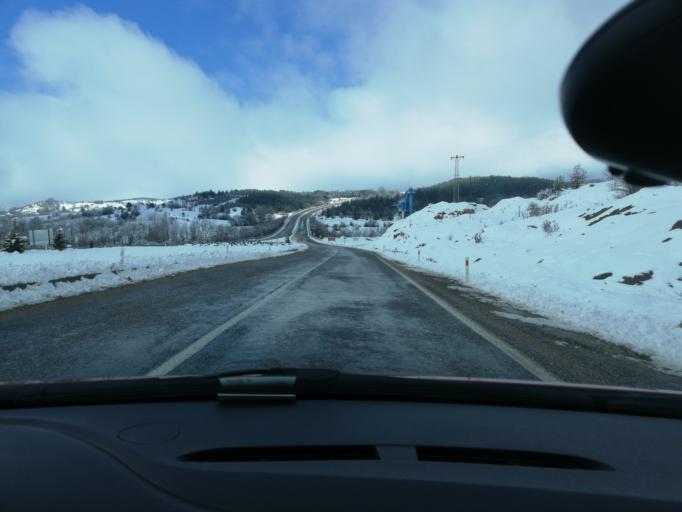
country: TR
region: Kastamonu
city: Ihsangazi
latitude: 41.3054
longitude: 33.5910
